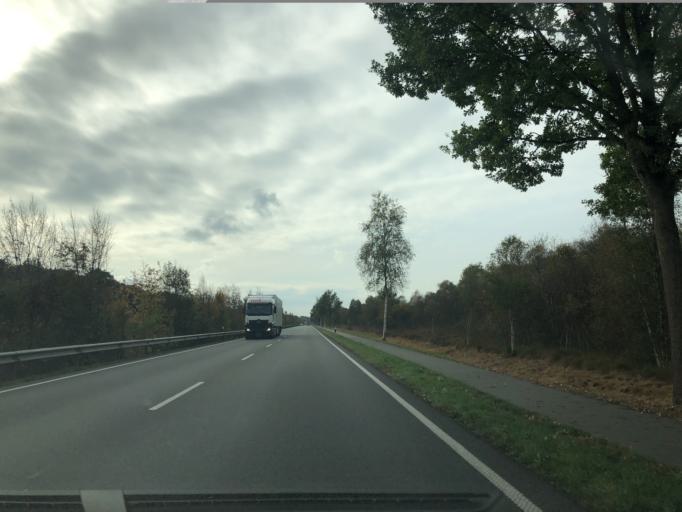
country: DE
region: Lower Saxony
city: Friesoythe
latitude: 53.0465
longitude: 7.7942
